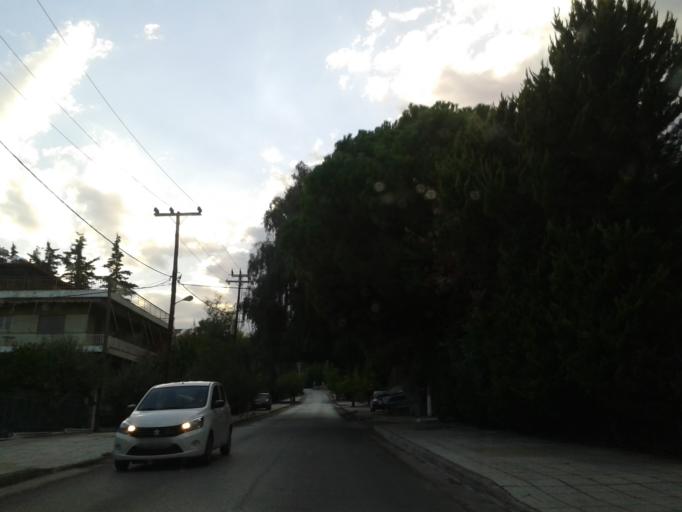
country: GR
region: Attica
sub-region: Nomarchia Anatolikis Attikis
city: Nea Makri
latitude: 38.0688
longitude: 23.9910
